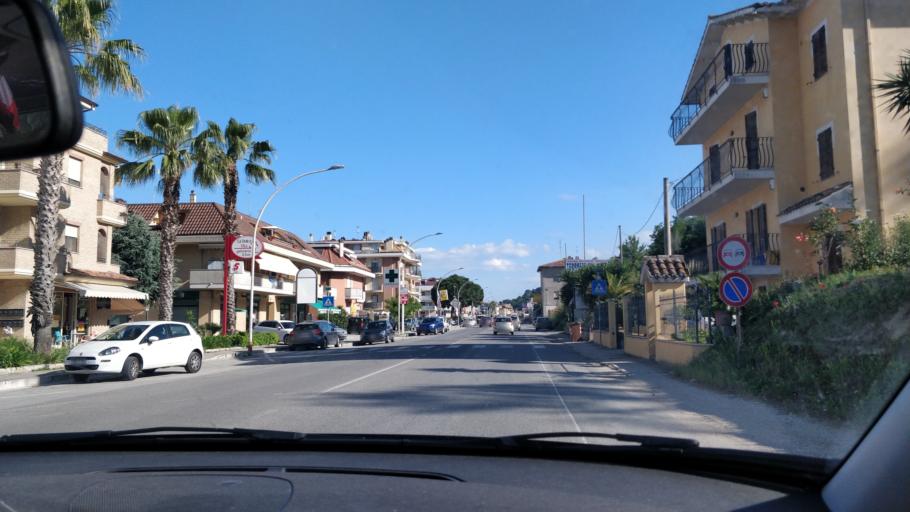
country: IT
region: The Marches
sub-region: Provincia di Ascoli Piceno
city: Cupra Marittima
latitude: 43.0329
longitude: 13.8564
